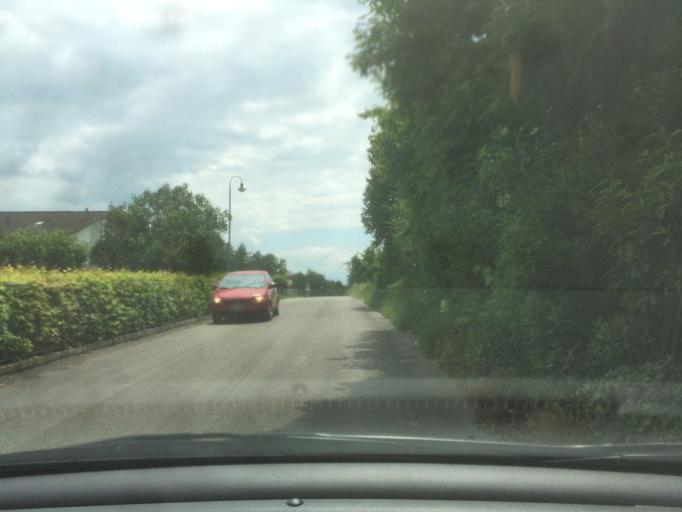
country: CH
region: Zurich
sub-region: Bezirk Pfaeffikon
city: Pfaeffikon / Pfaeffikon (Dorfkern)
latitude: 47.3539
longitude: 8.7666
